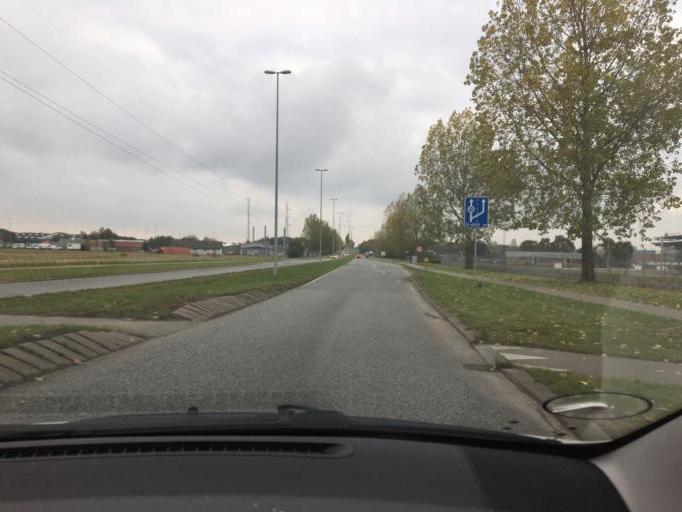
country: DK
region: South Denmark
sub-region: Fredericia Kommune
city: Fredericia
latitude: 55.5929
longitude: 9.7553
